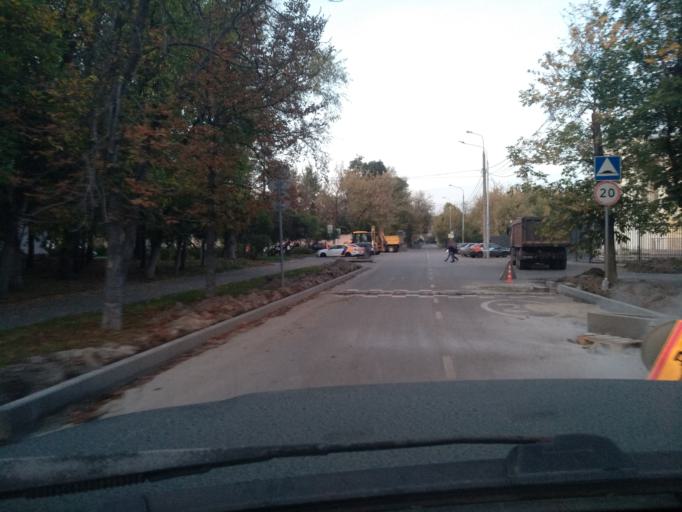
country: RU
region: Moskovskaya
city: Kur'yanovo
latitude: 55.6533
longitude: 37.7011
